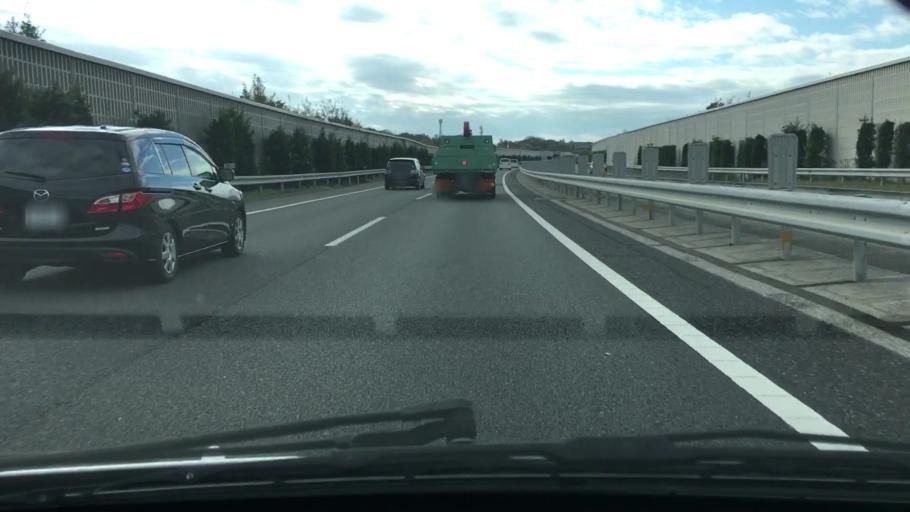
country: JP
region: Chiba
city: Chiba
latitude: 35.5461
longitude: 140.1410
